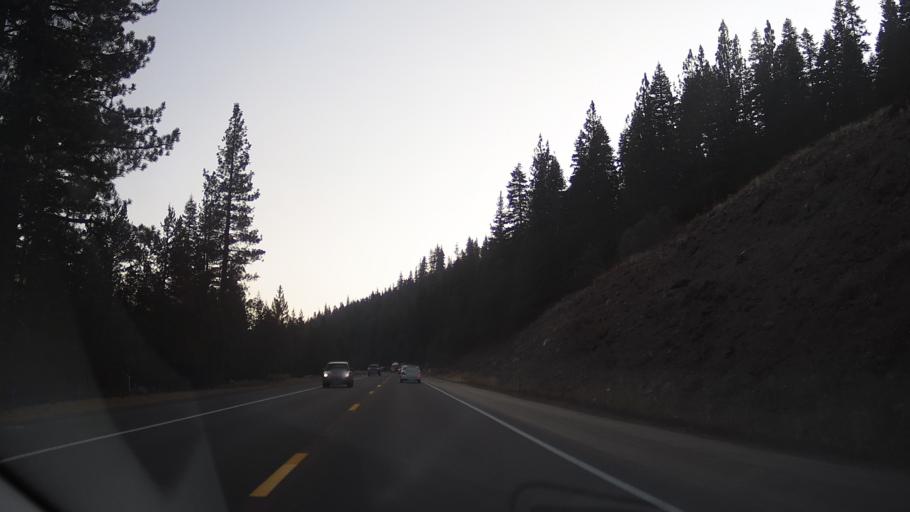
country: US
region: California
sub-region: Nevada County
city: Truckee
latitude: 39.2475
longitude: -120.2111
